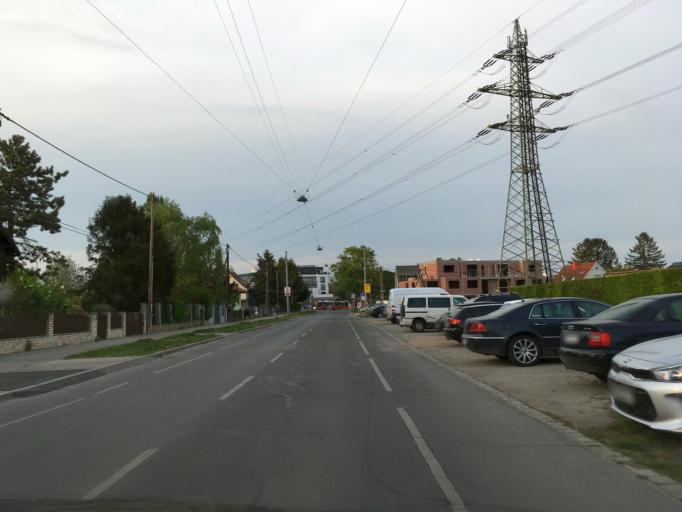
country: AT
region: Lower Austria
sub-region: Politischer Bezirk Wien-Umgebung
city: Gerasdorf bei Wien
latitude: 48.2848
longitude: 16.4289
